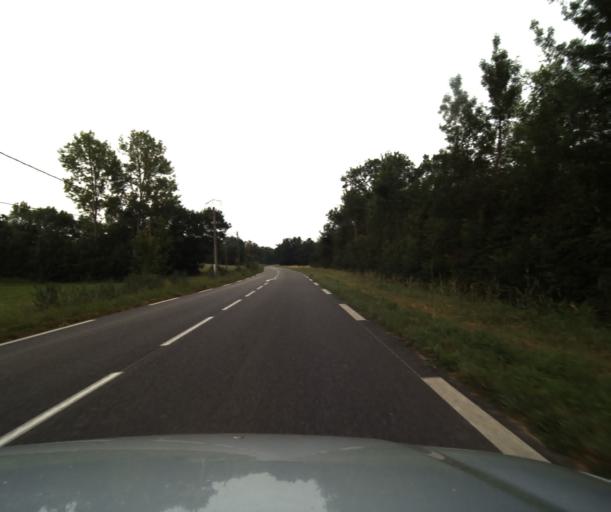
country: FR
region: Midi-Pyrenees
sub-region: Departement du Gers
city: Gimont
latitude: 43.7043
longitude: 0.8508
